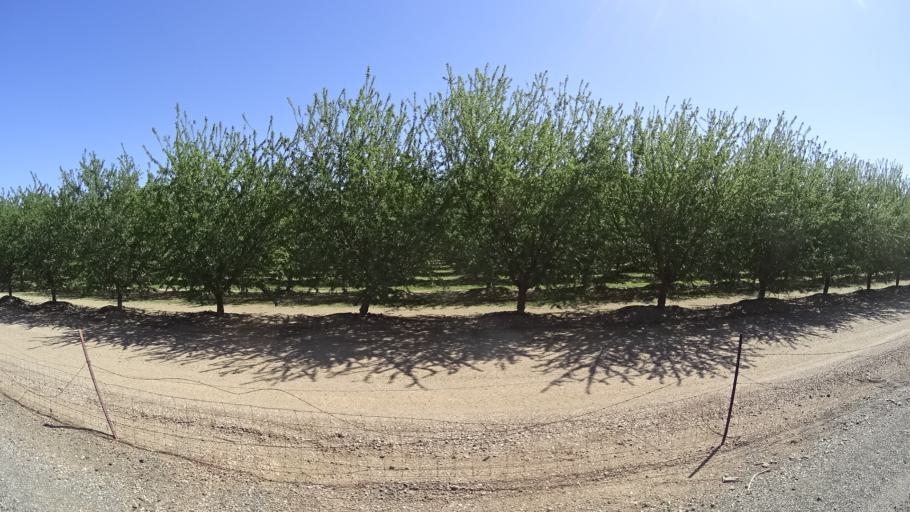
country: US
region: California
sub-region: Glenn County
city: Orland
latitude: 39.6604
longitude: -122.2532
